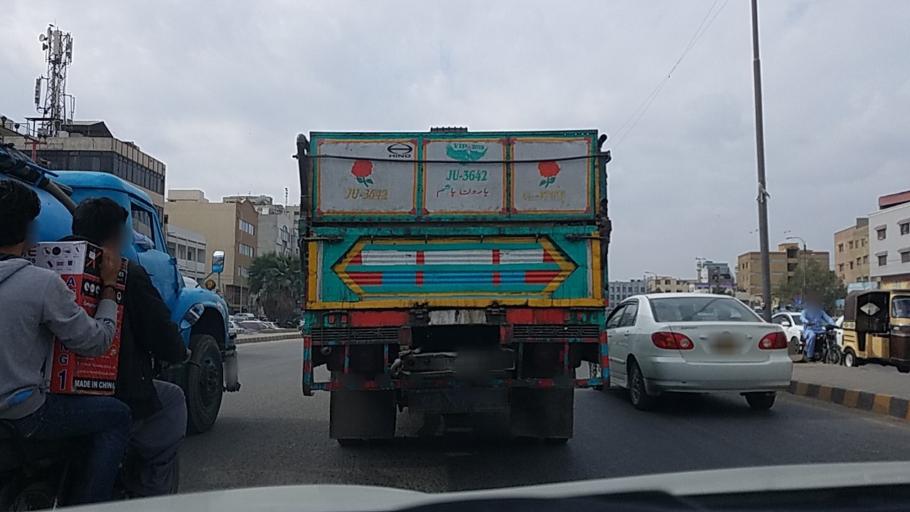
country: PK
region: Sindh
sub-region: Karachi District
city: Karachi
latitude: 24.8339
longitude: 67.0733
